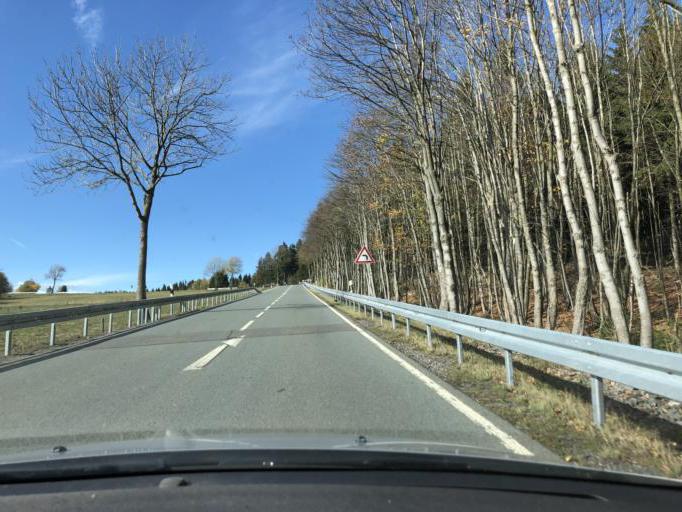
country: DE
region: Thuringia
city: Neuhaus am Rennweg
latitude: 50.5230
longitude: 11.1523
